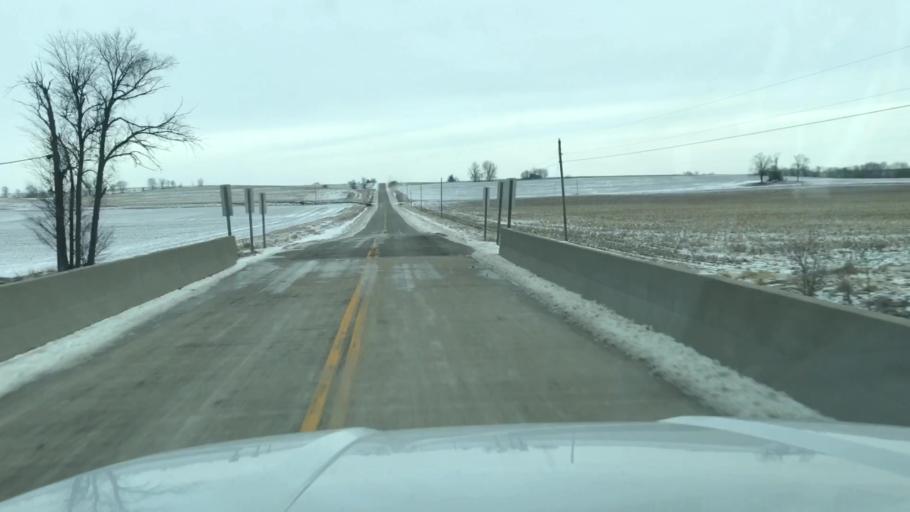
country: US
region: Missouri
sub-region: Holt County
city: Oregon
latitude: 40.0751
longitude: -94.9747
